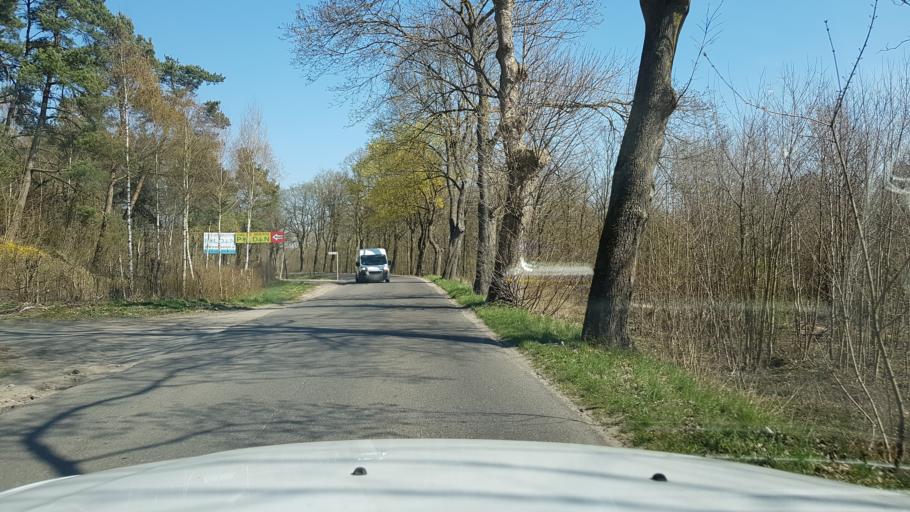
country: PL
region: West Pomeranian Voivodeship
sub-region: Powiat slawienski
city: Slawno
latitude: 54.3812
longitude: 16.6928
